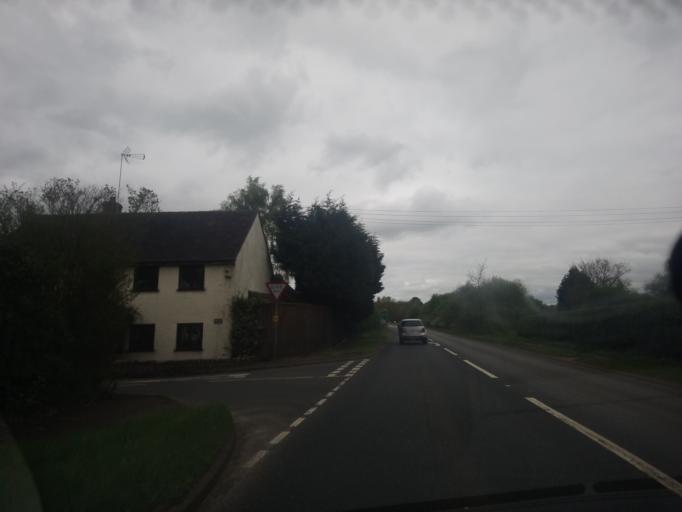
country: GB
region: England
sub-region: Telford and Wrekin
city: Chetwynd
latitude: 52.8281
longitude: -2.4549
